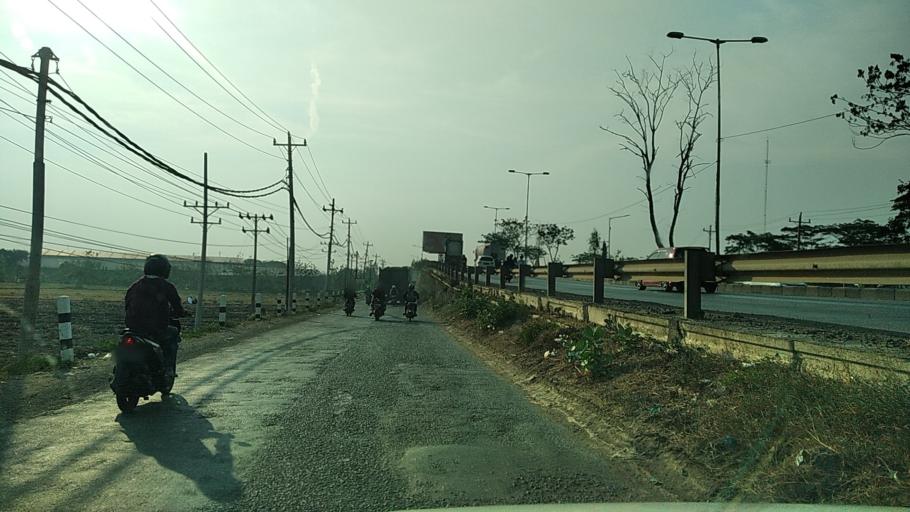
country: ID
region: Central Java
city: Semarang
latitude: -6.9676
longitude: 110.2827
